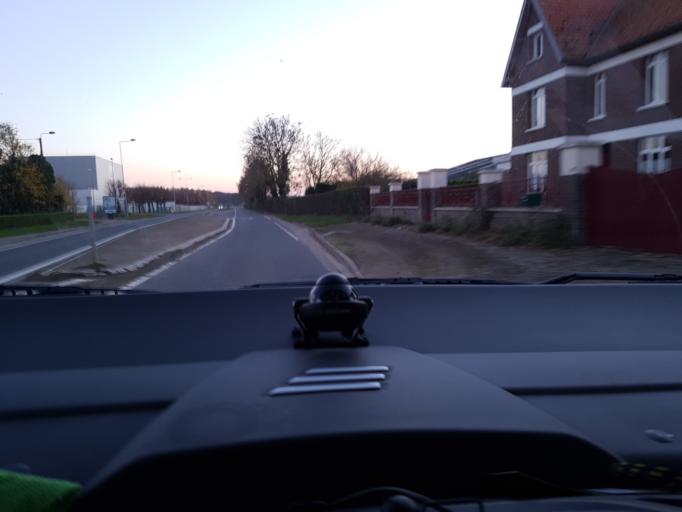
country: FR
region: Picardie
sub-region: Departement de la Somme
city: Rue
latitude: 50.3099
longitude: 1.7510
